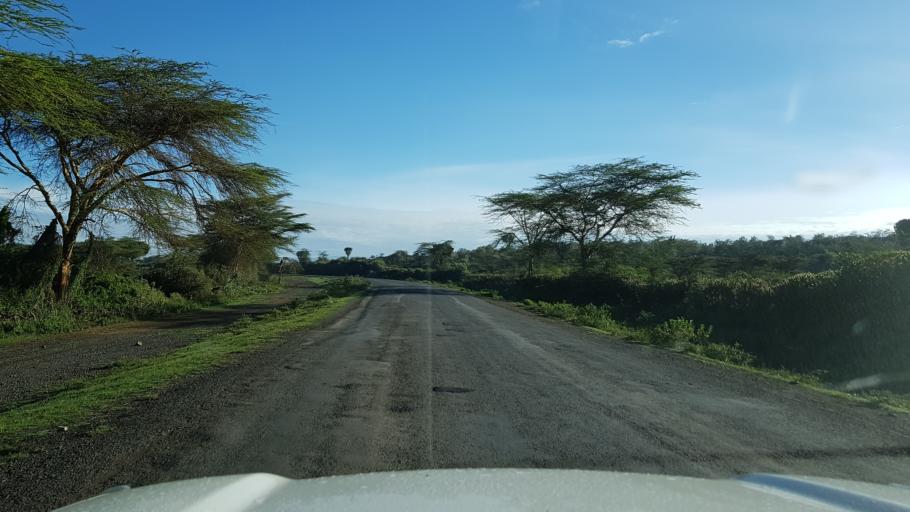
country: KE
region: Nakuru
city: Naivasha
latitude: -0.7894
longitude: 36.4252
